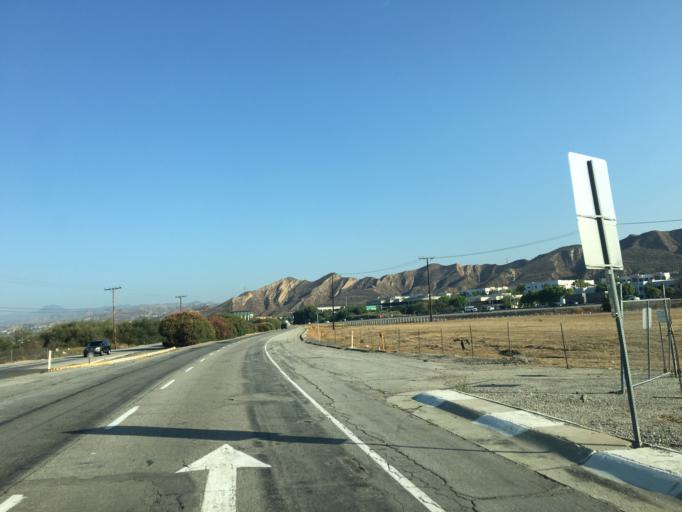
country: US
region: California
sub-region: Los Angeles County
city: Valencia
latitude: 34.4357
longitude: -118.5954
